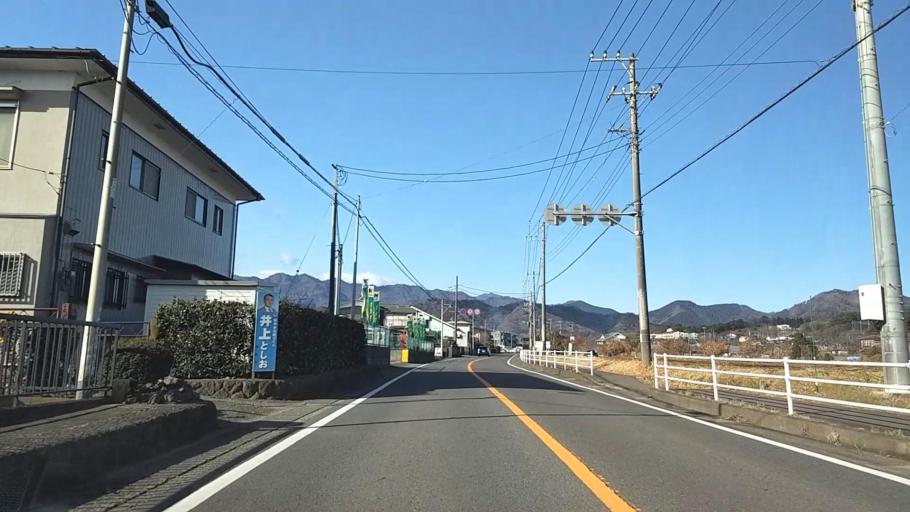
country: JP
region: Kanagawa
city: Atsugi
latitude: 35.4685
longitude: 139.3307
